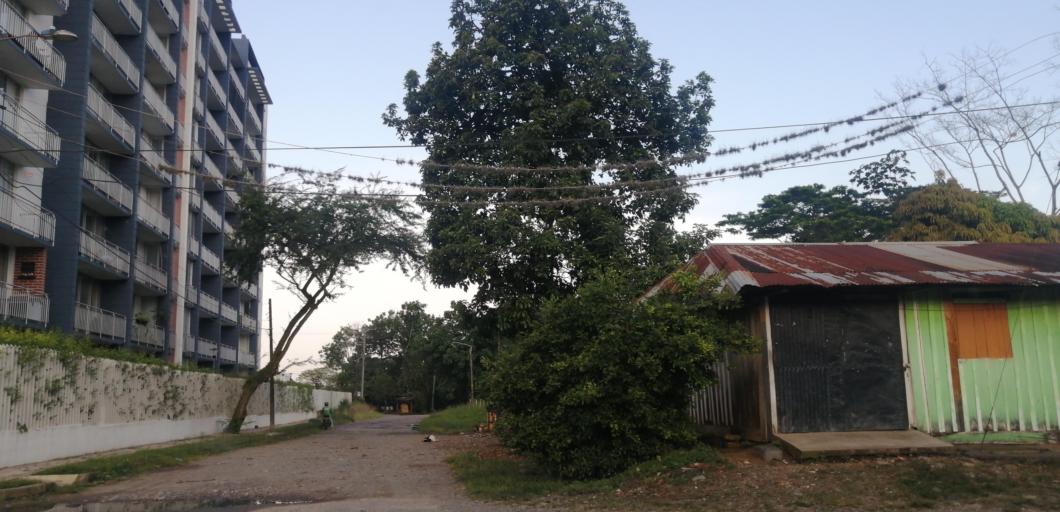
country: CO
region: Meta
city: Acacias
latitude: 3.9843
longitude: -73.7569
